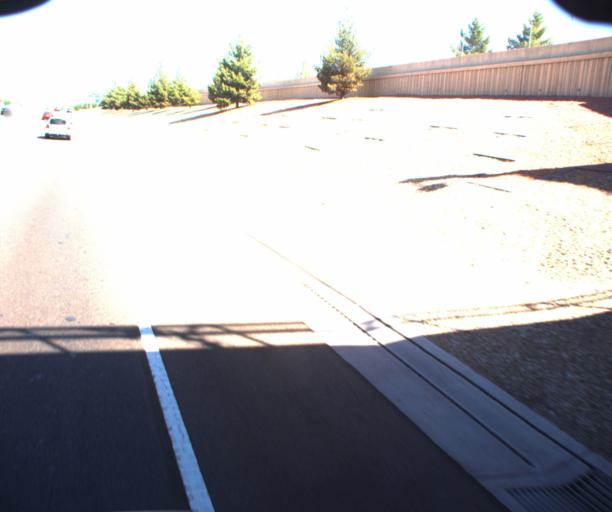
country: US
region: Arizona
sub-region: Maricopa County
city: San Carlos
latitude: 33.3351
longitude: -111.8928
